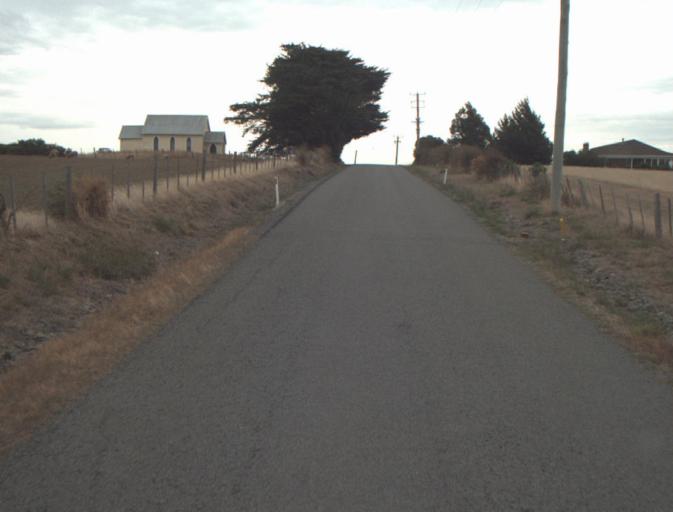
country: AU
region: Tasmania
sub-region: Northern Midlands
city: Evandale
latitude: -41.5167
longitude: 147.2526
